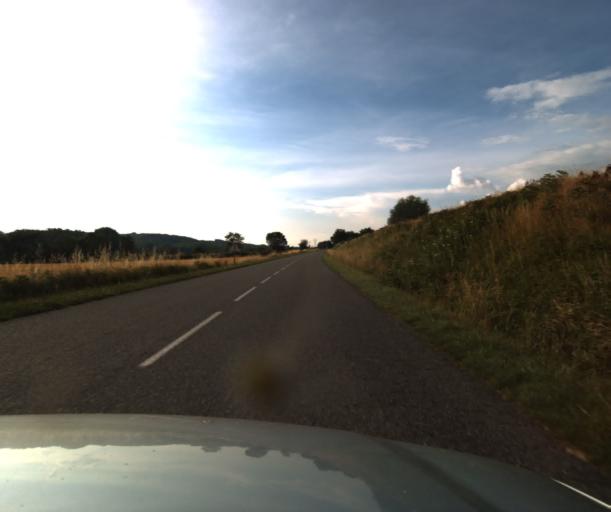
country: FR
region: Midi-Pyrenees
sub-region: Departement du Tarn-et-Garonne
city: Saint-Porquier
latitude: 43.9762
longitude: 1.1271
